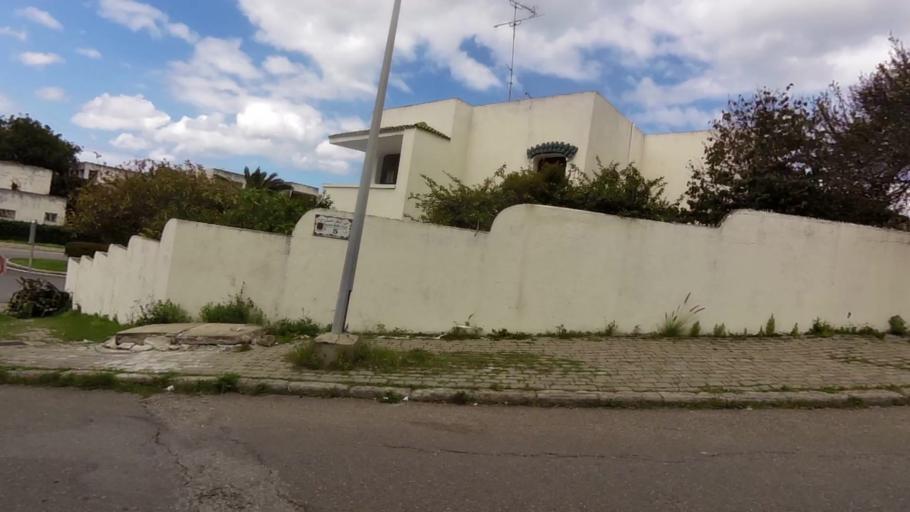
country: MA
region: Tanger-Tetouan
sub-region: Tanger-Assilah
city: Tangier
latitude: 35.7756
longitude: -5.7755
